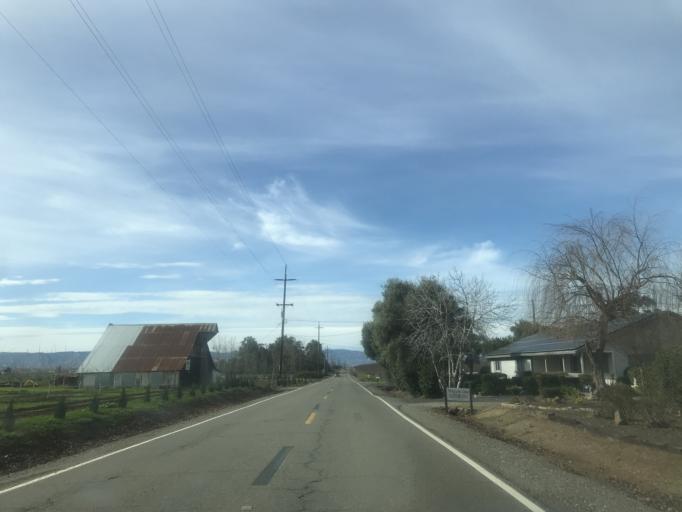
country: US
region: California
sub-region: Yolo County
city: Cottonwood
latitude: 38.6635
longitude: -121.8841
